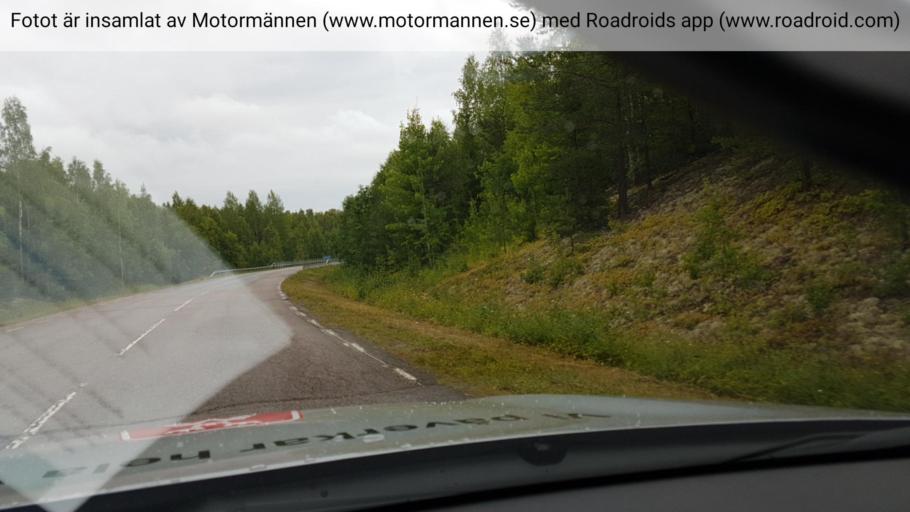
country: SE
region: Norrbotten
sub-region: Alvsbyns Kommun
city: AElvsbyn
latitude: 66.0836
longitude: 20.9019
